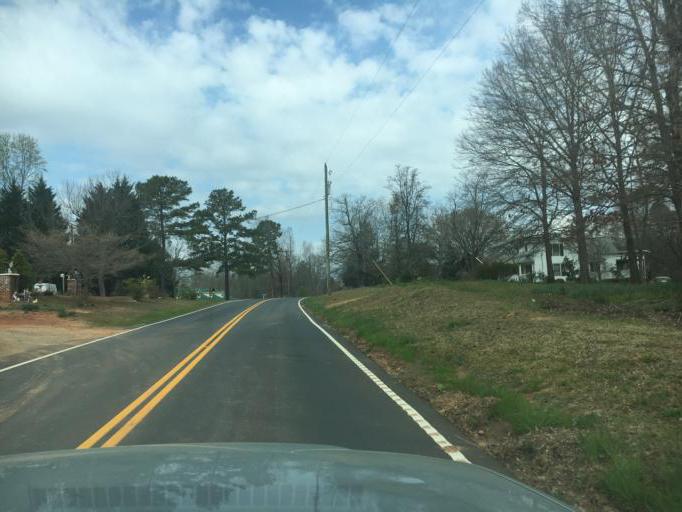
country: US
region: South Carolina
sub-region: Spartanburg County
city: Landrum
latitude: 35.0943
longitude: -82.2024
